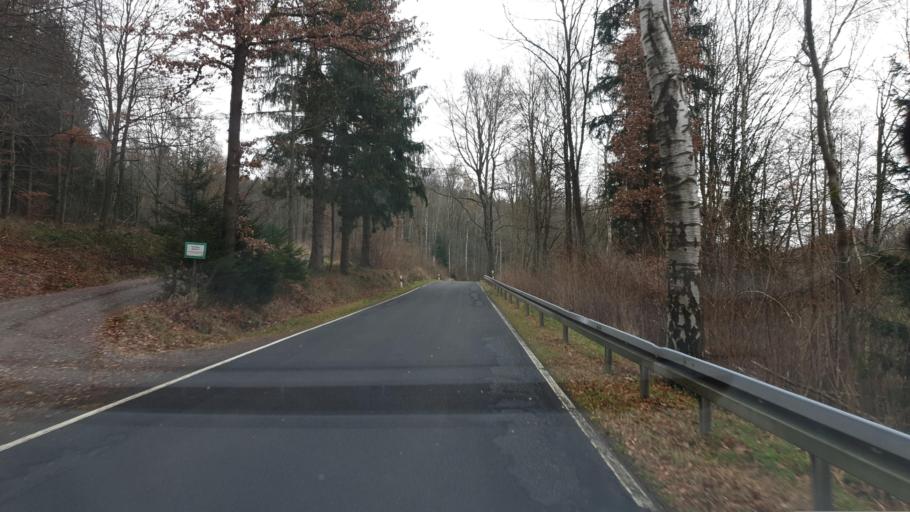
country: DE
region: Saxony
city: Mulda
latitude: 50.7980
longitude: 13.4054
